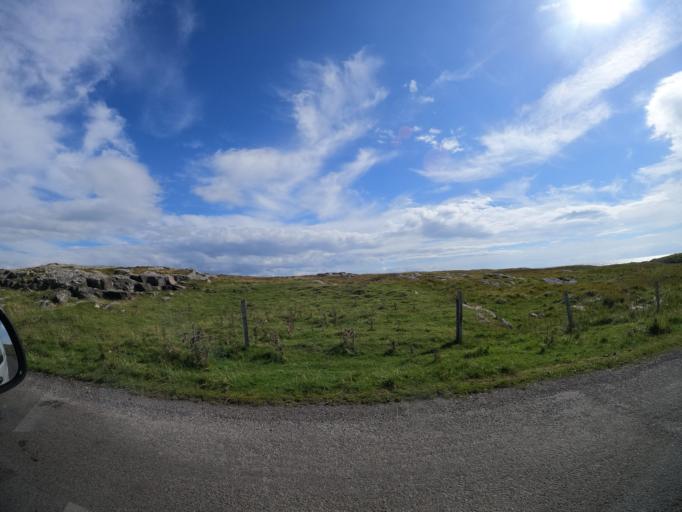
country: GB
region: Scotland
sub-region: Eilean Siar
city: Barra
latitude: 56.5055
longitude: -6.8018
